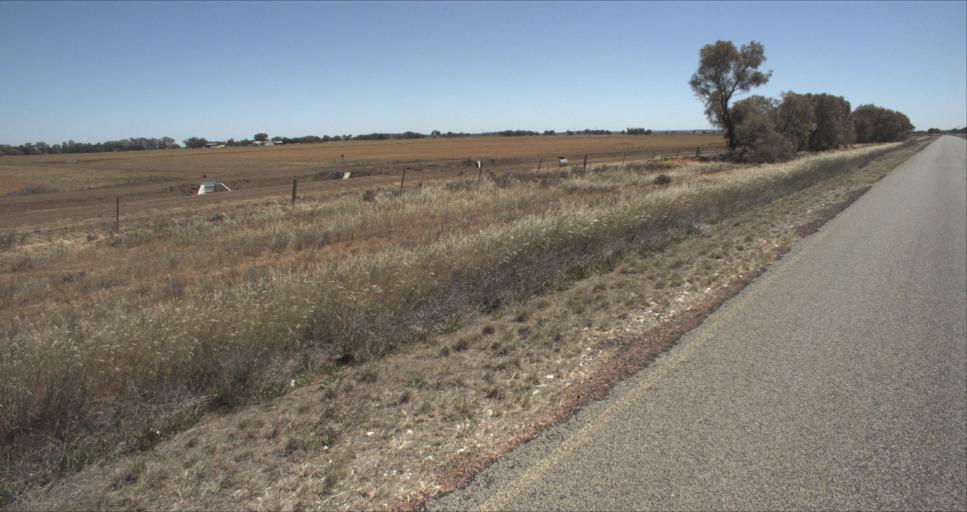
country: AU
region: New South Wales
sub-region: Leeton
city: Leeton
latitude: -34.4617
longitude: 146.2940
